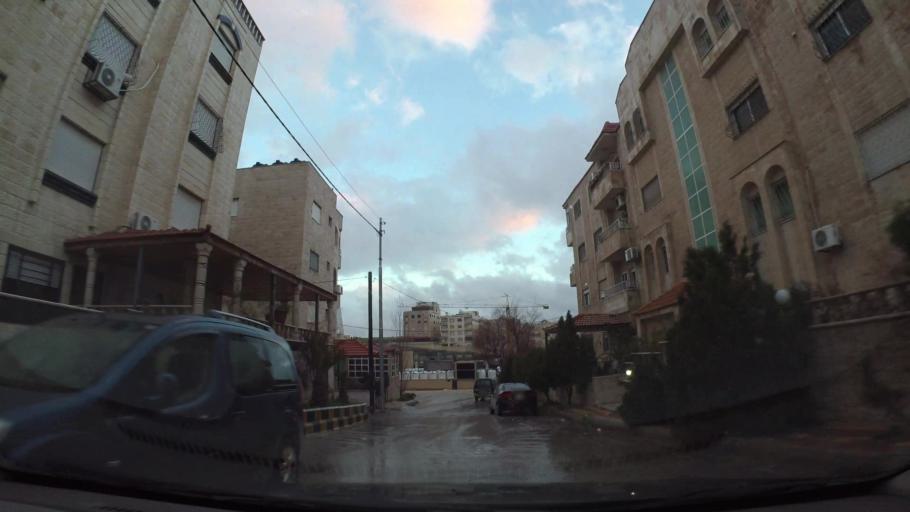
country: JO
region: Amman
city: Amman
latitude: 31.9950
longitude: 35.9214
